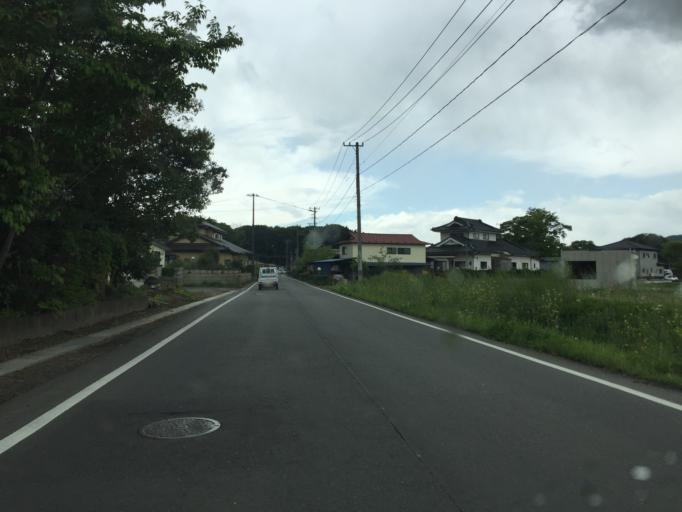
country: JP
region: Fukushima
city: Ishikawa
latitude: 37.1355
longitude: 140.3294
